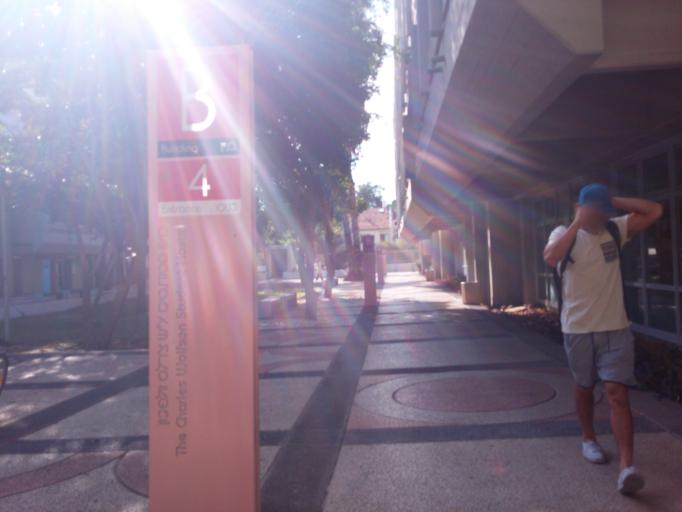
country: IL
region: Tel Aviv
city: Ramat Gan
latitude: 32.1121
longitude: 34.8010
